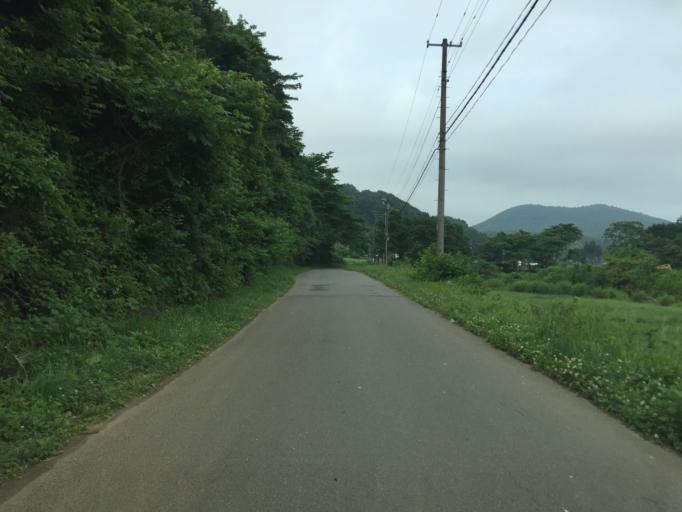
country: JP
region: Fukushima
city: Yanagawamachi-saiwaicho
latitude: 37.7823
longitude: 140.7162
